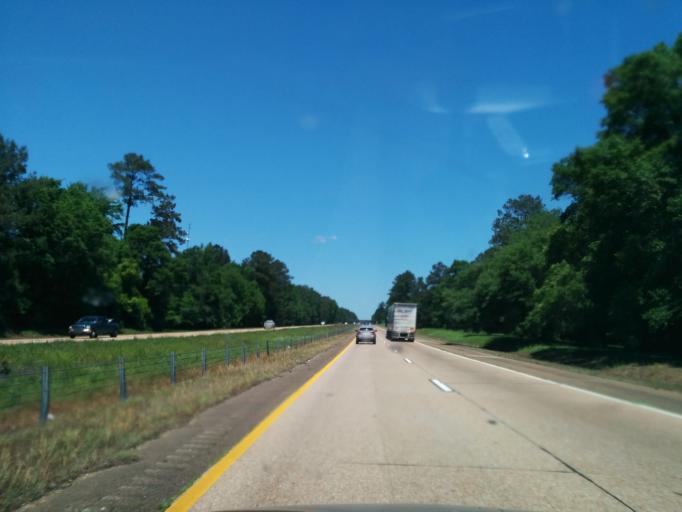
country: US
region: Mississippi
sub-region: Pike County
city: Magnolia
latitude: 31.1235
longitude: -90.4832
